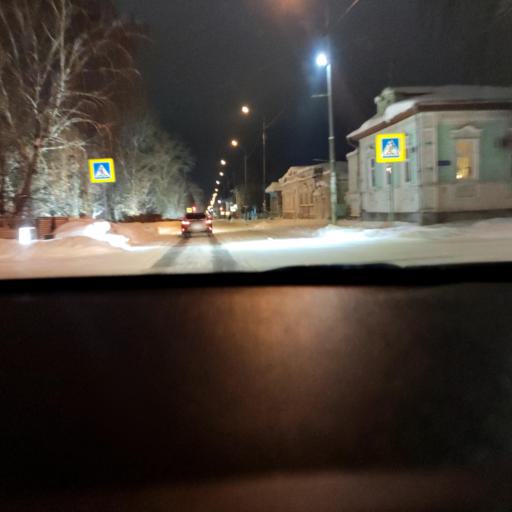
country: RU
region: Tatarstan
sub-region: Chistopol'skiy Rayon
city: Chistopol'
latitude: 55.3660
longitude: 50.6439
